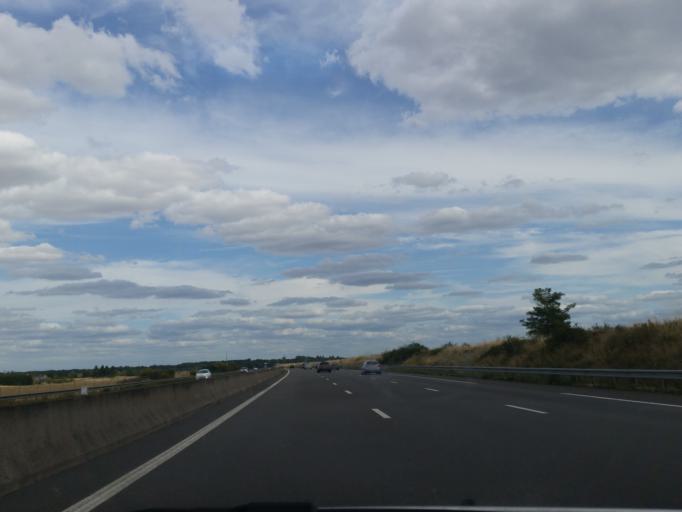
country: FR
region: Centre
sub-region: Departement du Loir-et-Cher
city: Herbault
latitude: 47.6162
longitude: 1.1985
